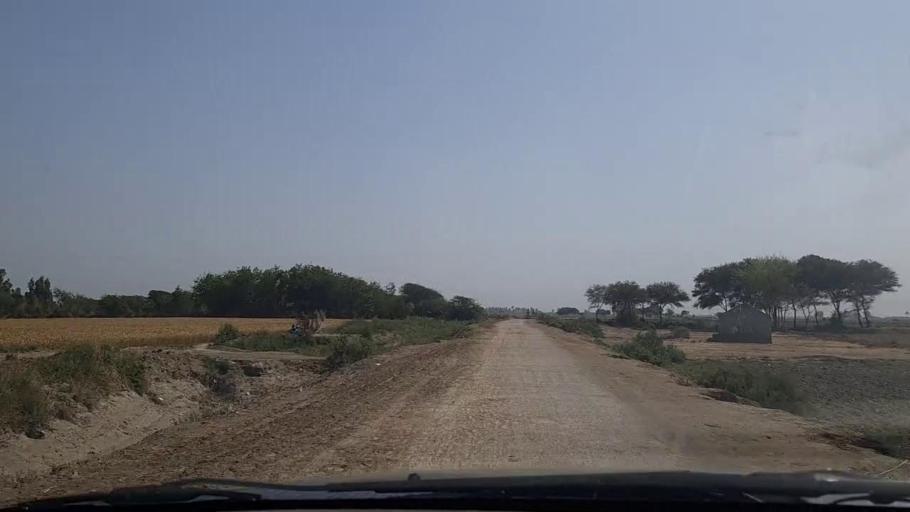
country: PK
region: Sindh
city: Keti Bandar
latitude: 24.2708
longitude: 67.6724
